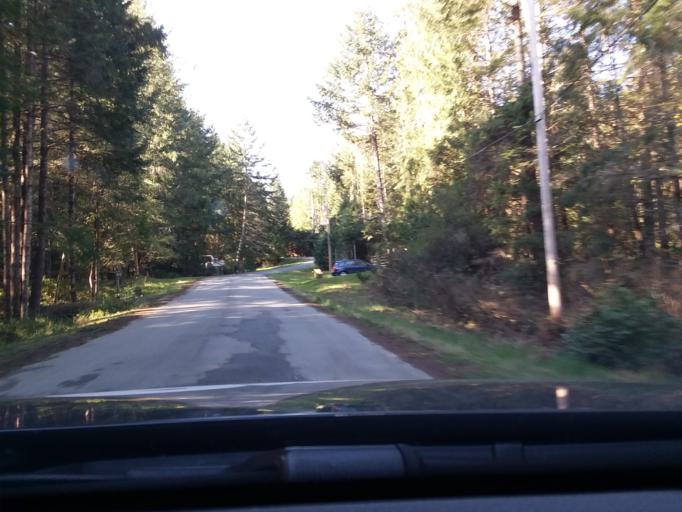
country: CA
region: British Columbia
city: North Saanich
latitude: 48.8757
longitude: -123.3246
